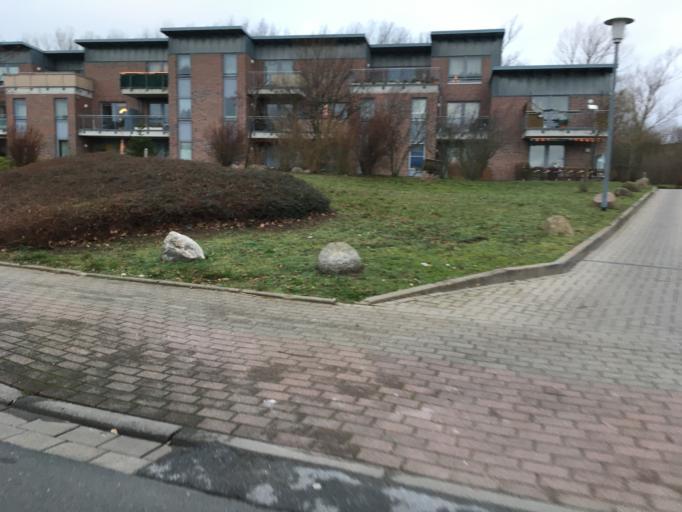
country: DE
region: Mecklenburg-Vorpommern
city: Sassnitz
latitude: 54.5106
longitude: 13.6133
